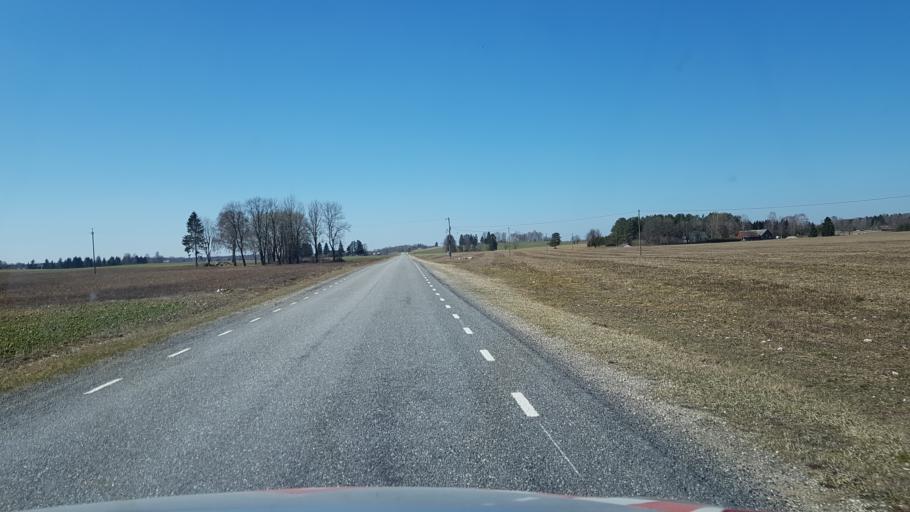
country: EE
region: Laeaene-Virumaa
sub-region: Rakke vald
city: Rakke
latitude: 59.0081
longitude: 26.1550
